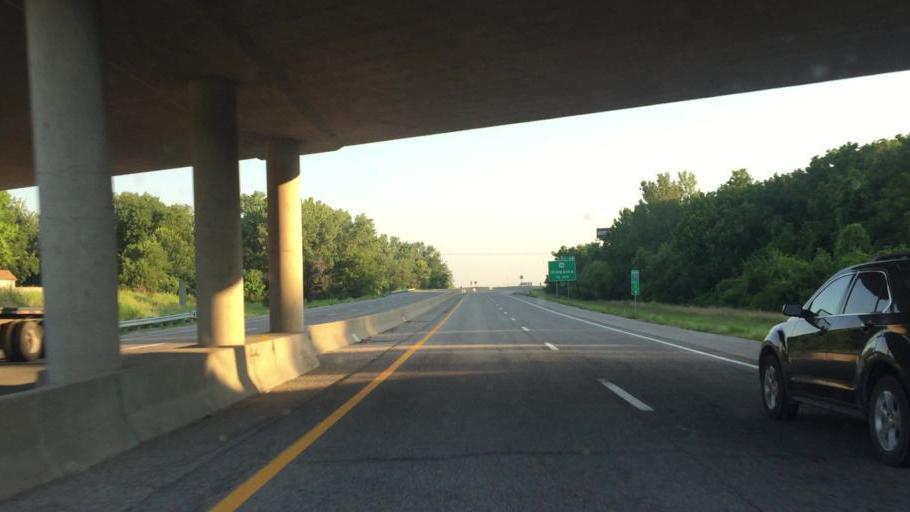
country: US
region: Kansas
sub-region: Doniphan County
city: Elwood
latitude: 39.7336
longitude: -94.8486
